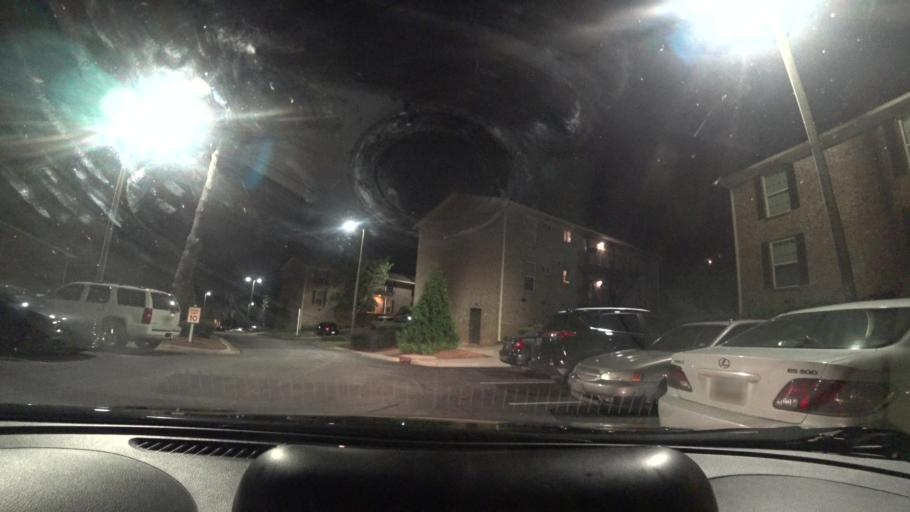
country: US
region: Georgia
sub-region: DeKalb County
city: Gresham Park
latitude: 33.7162
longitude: -84.3263
